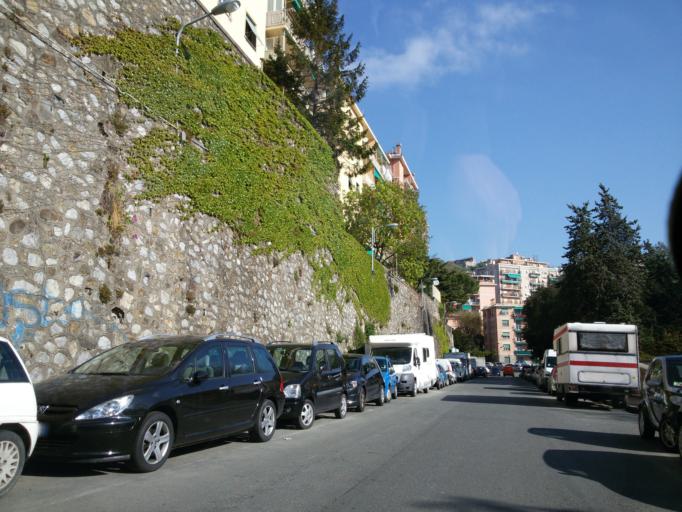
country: IT
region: Liguria
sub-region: Provincia di Genova
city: Genoa
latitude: 44.4064
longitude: 8.9778
